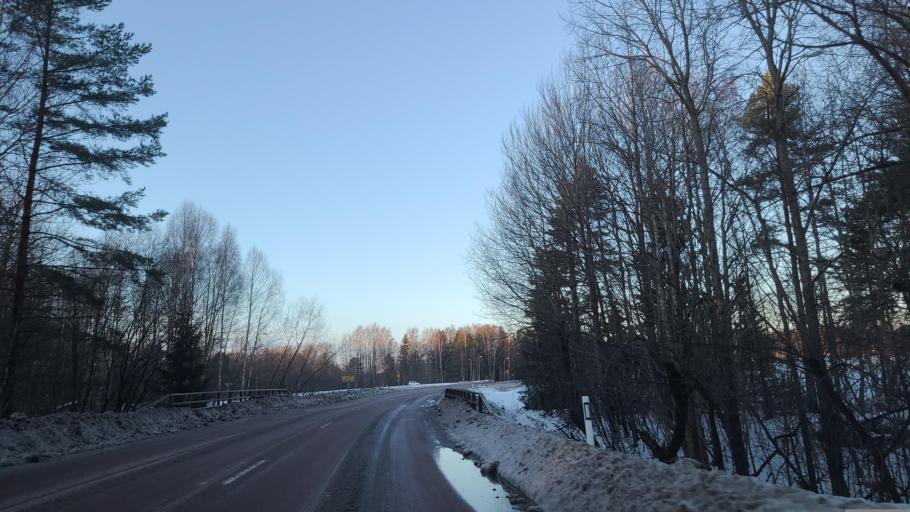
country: SE
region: Gaevleborg
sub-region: Soderhamns Kommun
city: Soderhamn
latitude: 61.2786
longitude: 16.9735
